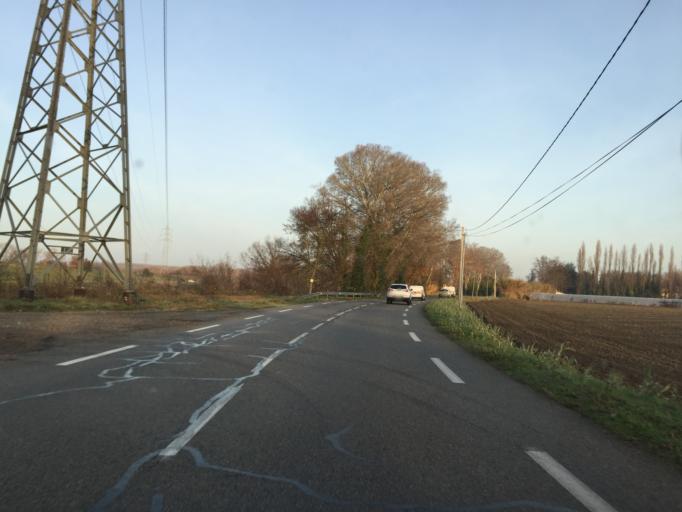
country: FR
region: Languedoc-Roussillon
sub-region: Departement du Gard
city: Montfaucon
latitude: 44.0798
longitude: 4.7618
